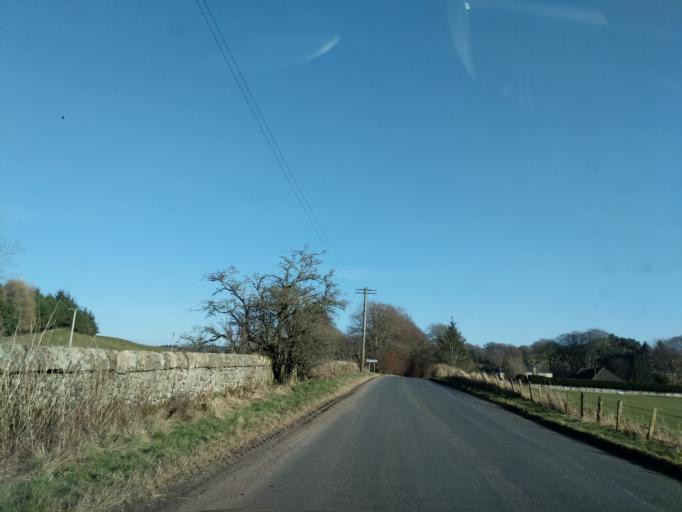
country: GB
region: Scotland
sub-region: The Scottish Borders
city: West Linton
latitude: 55.7176
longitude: -3.4224
